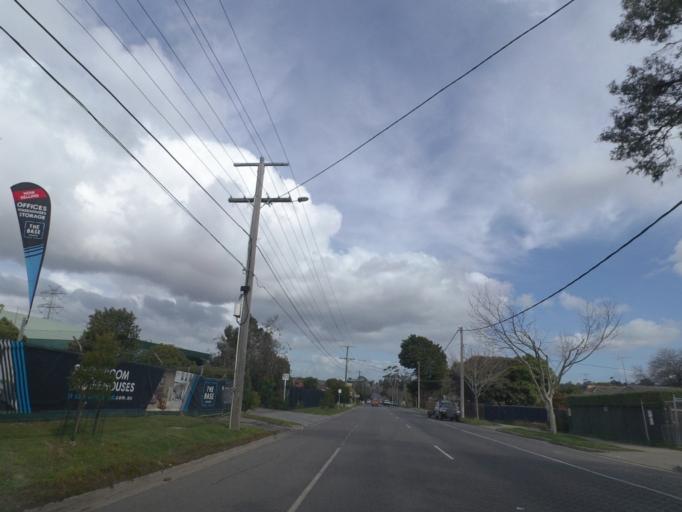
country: AU
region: Victoria
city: Mitcham
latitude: -37.8262
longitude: 145.2134
